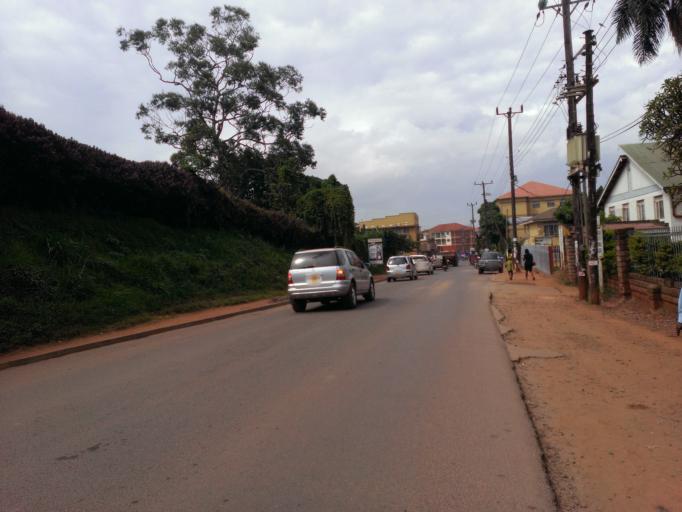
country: UG
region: Central Region
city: Kampala Central Division
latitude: 0.3125
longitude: 32.5574
